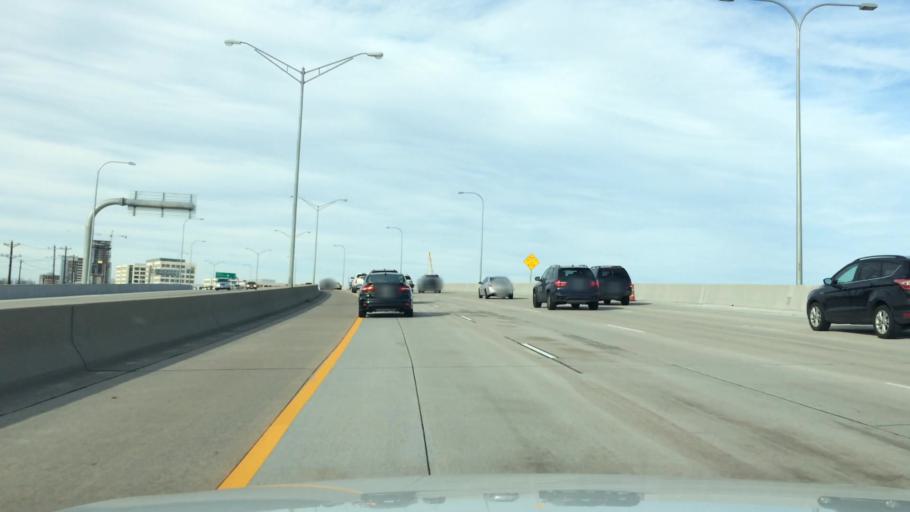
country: US
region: Texas
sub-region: Denton County
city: The Colony
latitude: 33.0633
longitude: -96.8255
